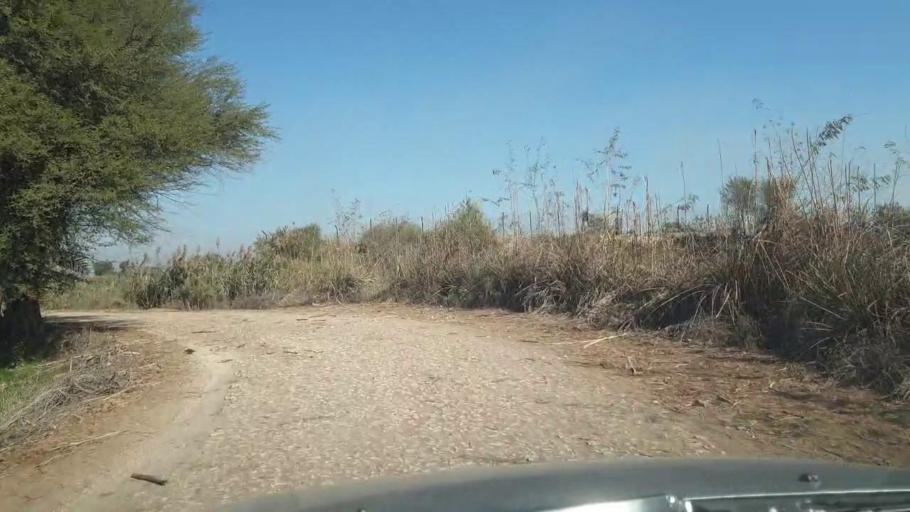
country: PK
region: Sindh
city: Ghotki
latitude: 28.0861
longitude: 69.3432
